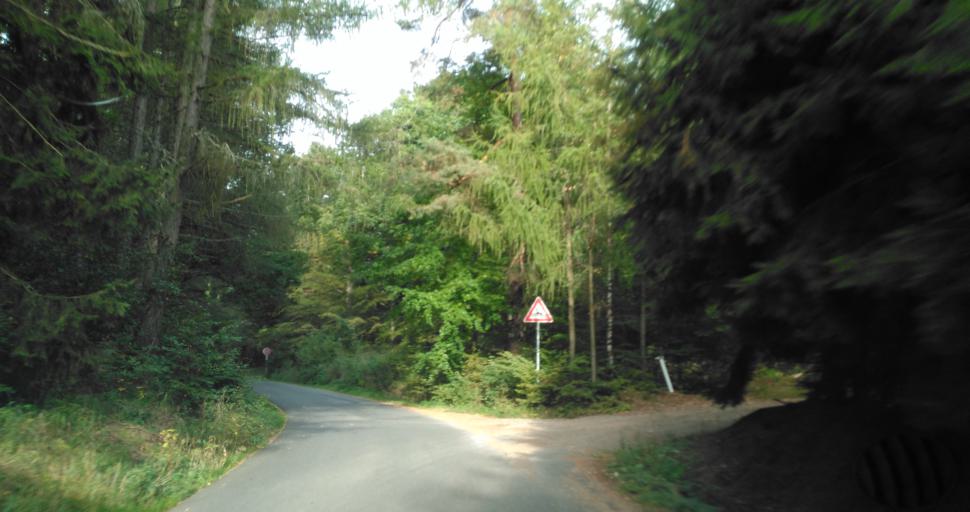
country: CZ
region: Plzensky
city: Zbiroh
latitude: 49.9245
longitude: 13.8037
